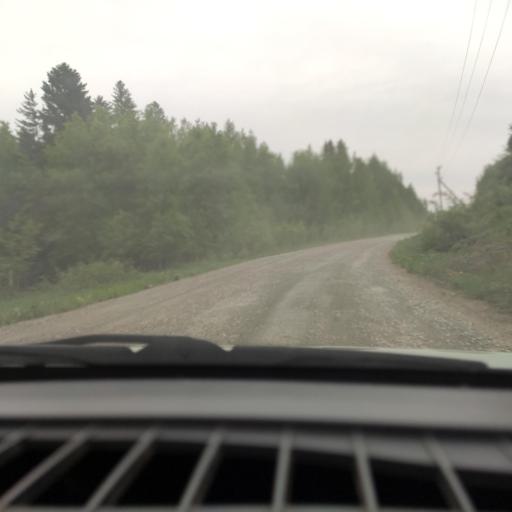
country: RU
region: Perm
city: Novyye Lyady
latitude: 57.9146
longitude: 56.6565
